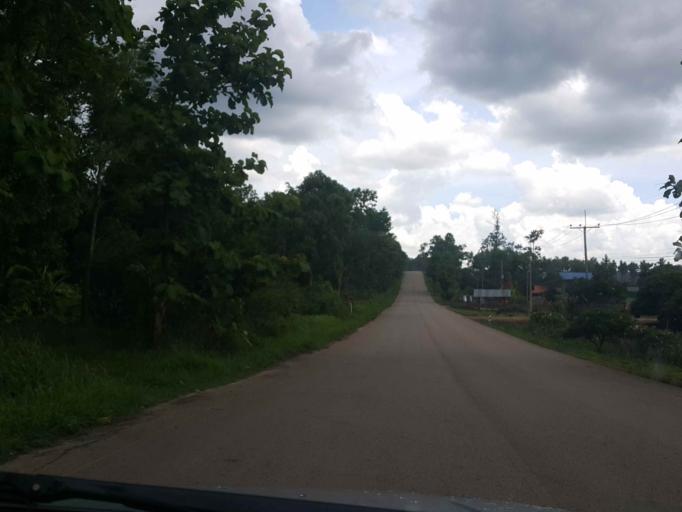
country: TH
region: Phayao
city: Dok Kham Tai
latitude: 18.9766
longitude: 100.0716
